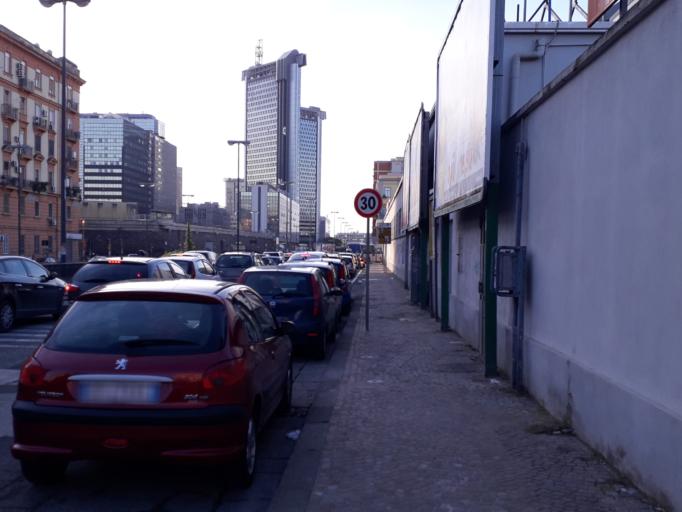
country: IT
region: Campania
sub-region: Provincia di Napoli
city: Napoli
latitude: 40.8608
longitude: 14.2762
